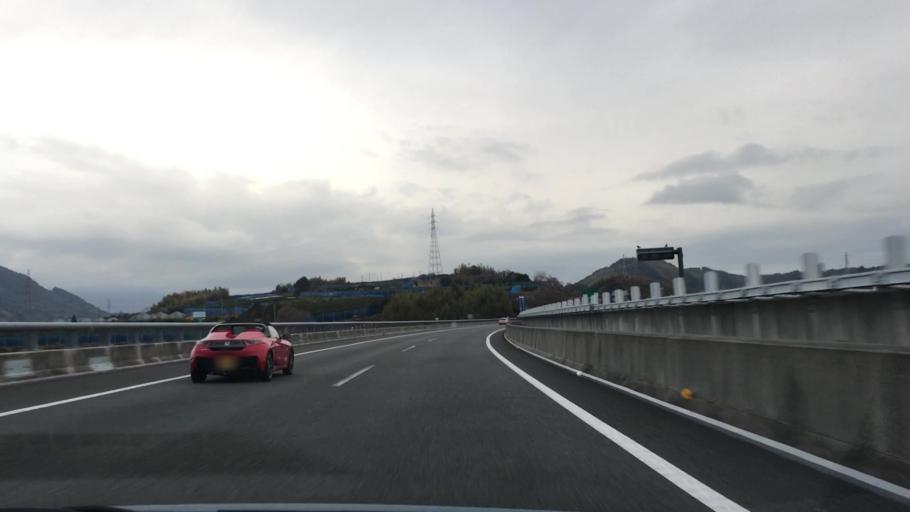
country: JP
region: Shizuoka
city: Shizuoka-shi
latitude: 35.0567
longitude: 138.4814
